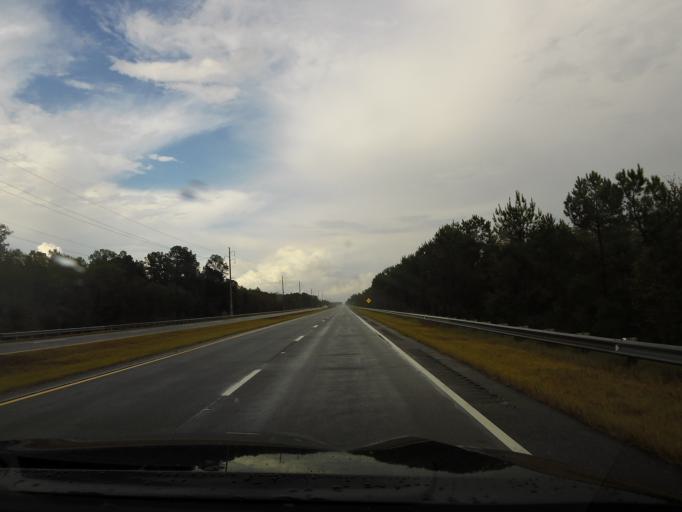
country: US
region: Georgia
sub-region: Long County
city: Ludowici
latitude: 31.6925
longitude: -81.7844
